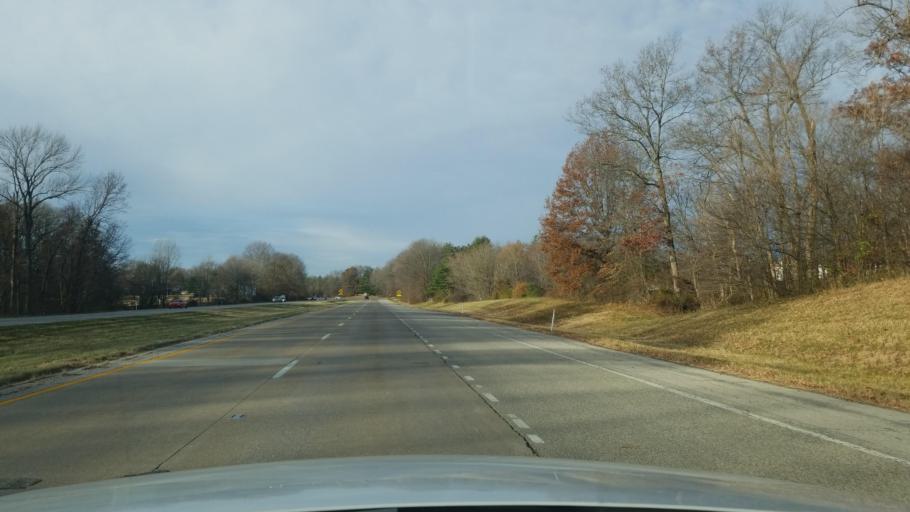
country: US
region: Indiana
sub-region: Vanderburgh County
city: Evansville
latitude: 37.9662
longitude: -87.6814
